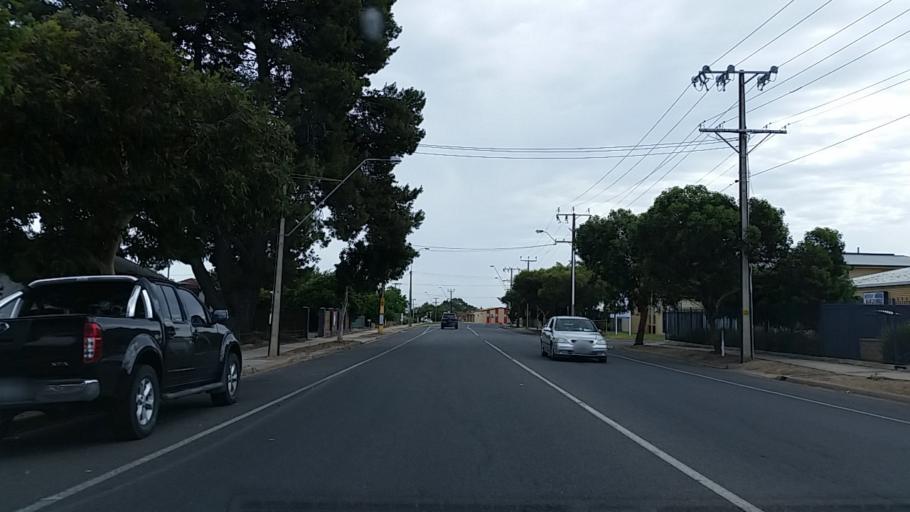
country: AU
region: South Australia
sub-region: Murray Bridge
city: Murray Bridge
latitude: -35.1304
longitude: 139.2800
